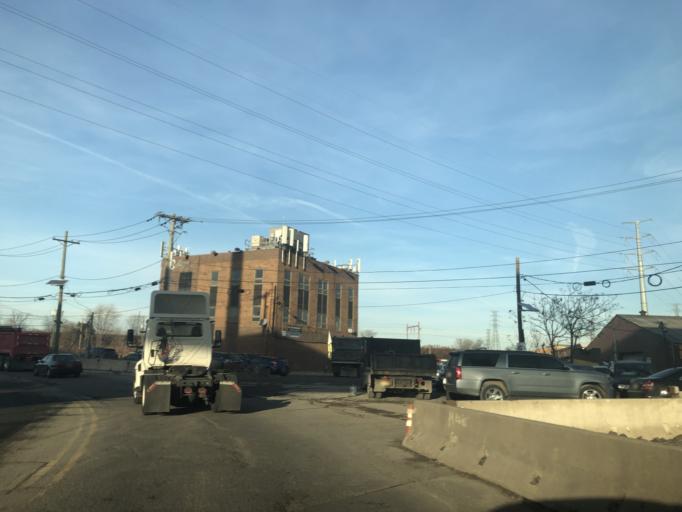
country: US
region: New Jersey
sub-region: Hudson County
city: Jersey City
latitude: 40.7421
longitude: -74.0828
